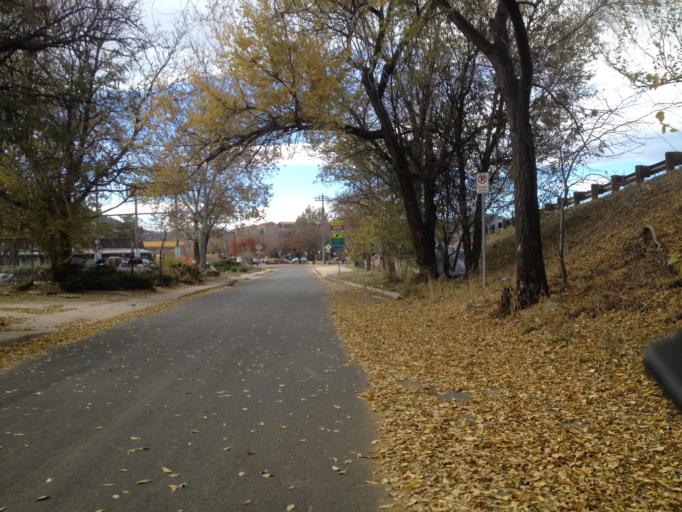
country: US
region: Colorado
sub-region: Boulder County
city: Boulder
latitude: 39.9995
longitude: -105.2581
